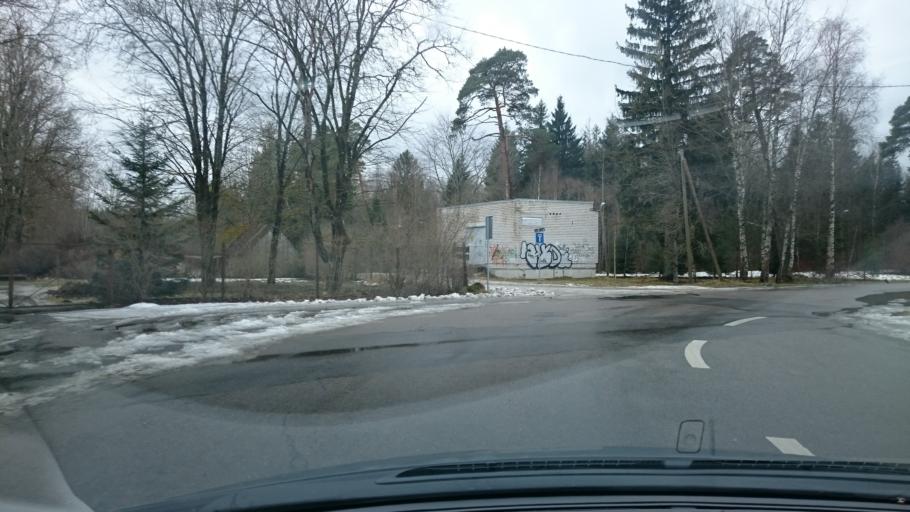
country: EE
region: Harju
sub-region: Saku vald
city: Saku
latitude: 59.3009
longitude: 24.6758
